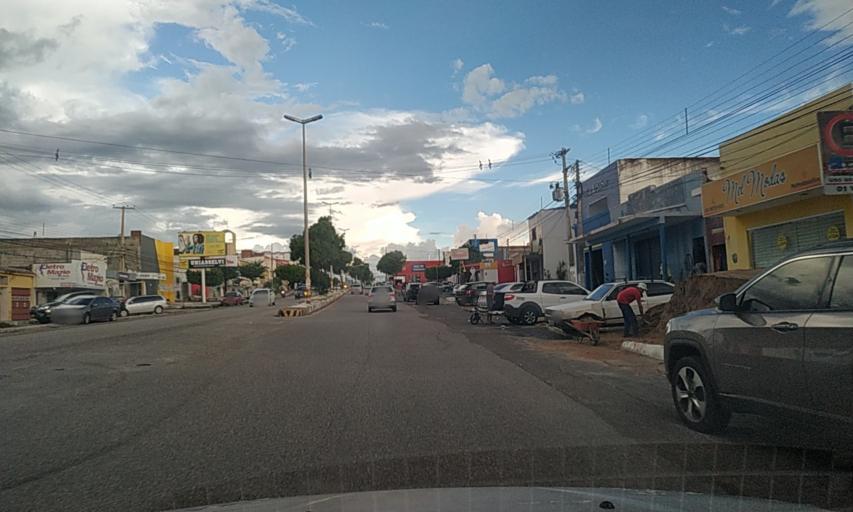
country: BR
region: Rio Grande do Norte
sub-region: Mossoro
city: Mossoro
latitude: -5.2056
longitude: -37.3361
